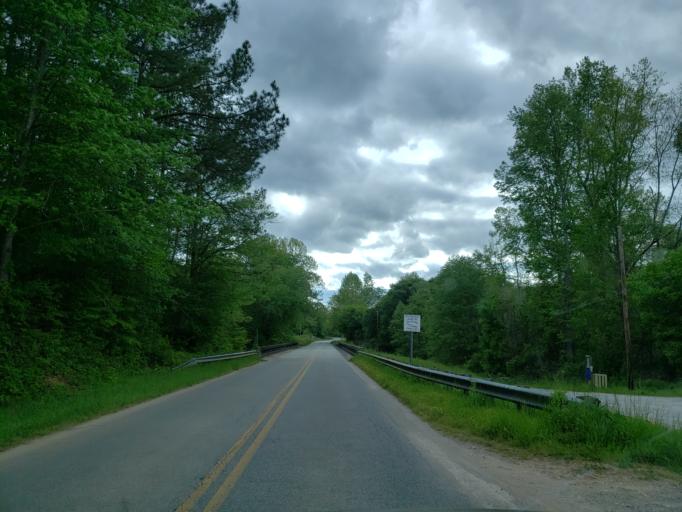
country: US
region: Georgia
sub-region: Haralson County
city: Tallapoosa
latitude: 33.7661
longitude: -85.3220
